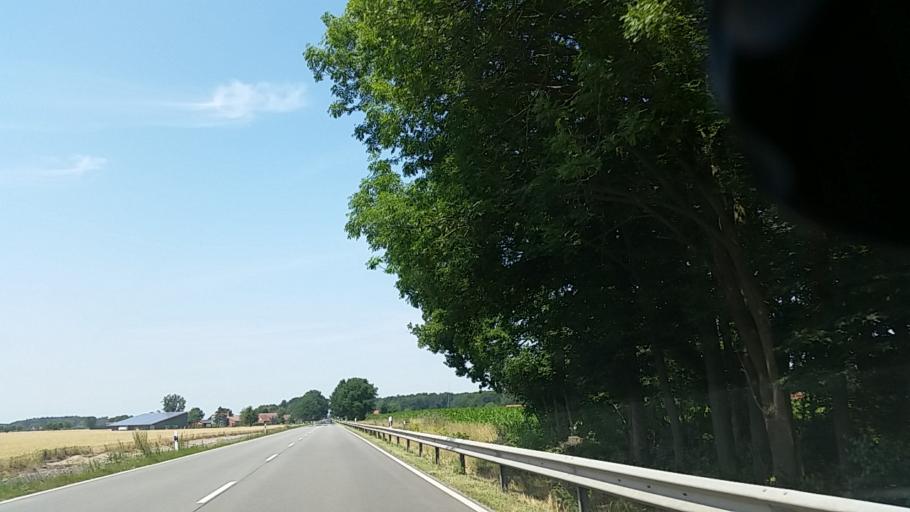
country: DE
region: Lower Saxony
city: Asendorf
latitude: 52.7866
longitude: 8.9919
